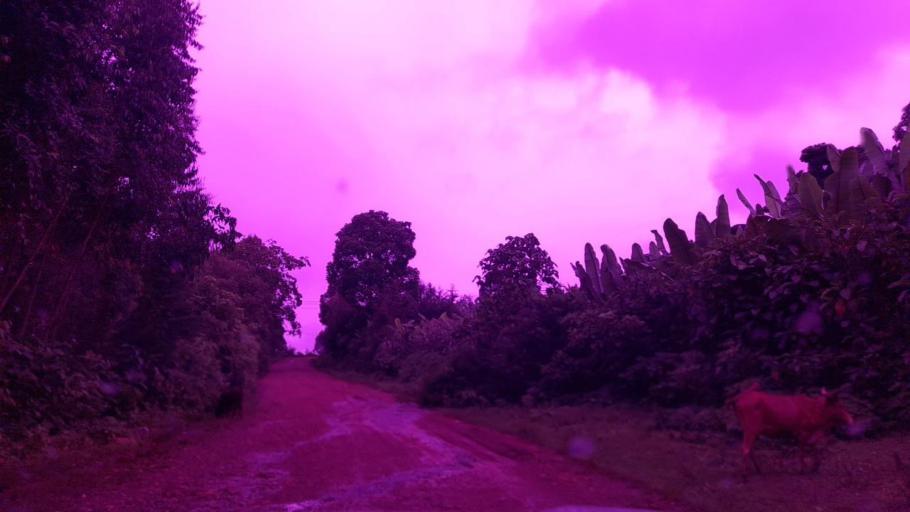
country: ET
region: Southern Nations, Nationalities, and People's Region
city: Tippi
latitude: 7.5802
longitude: 35.7761
